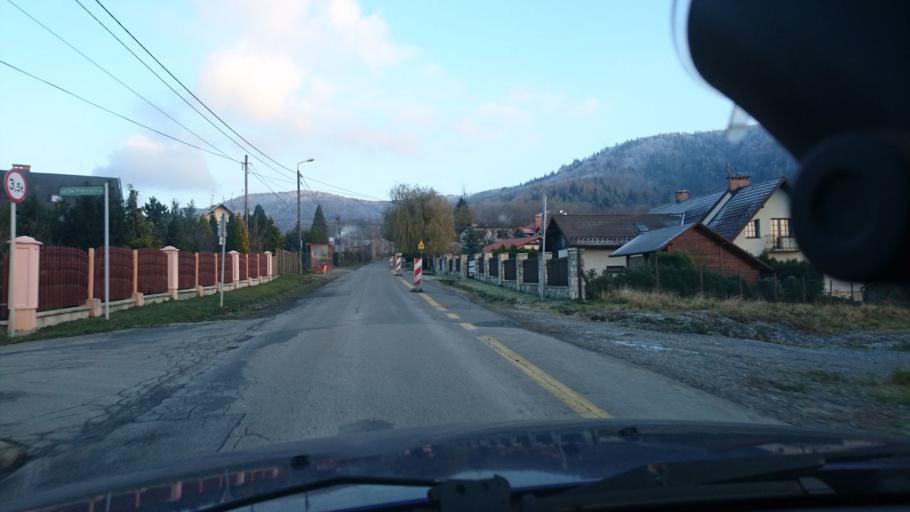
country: PL
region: Silesian Voivodeship
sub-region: Powiat bielski
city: Kozy
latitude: 49.8203
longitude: 19.1091
